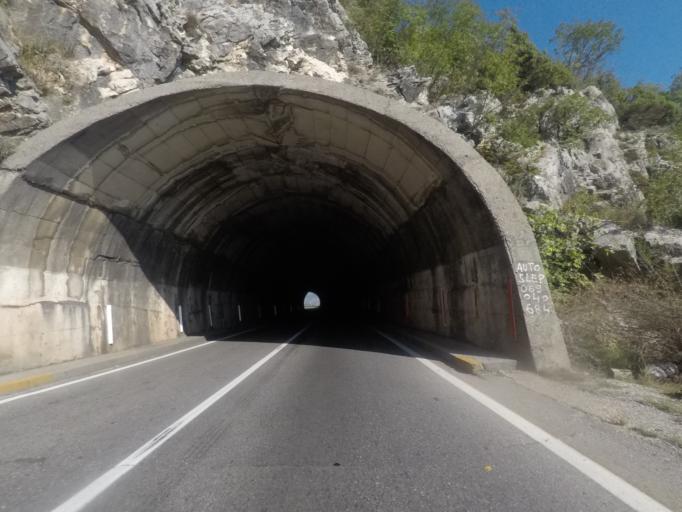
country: ME
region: Opstina Niksic
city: Niksic
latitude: 42.6330
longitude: 19.0069
